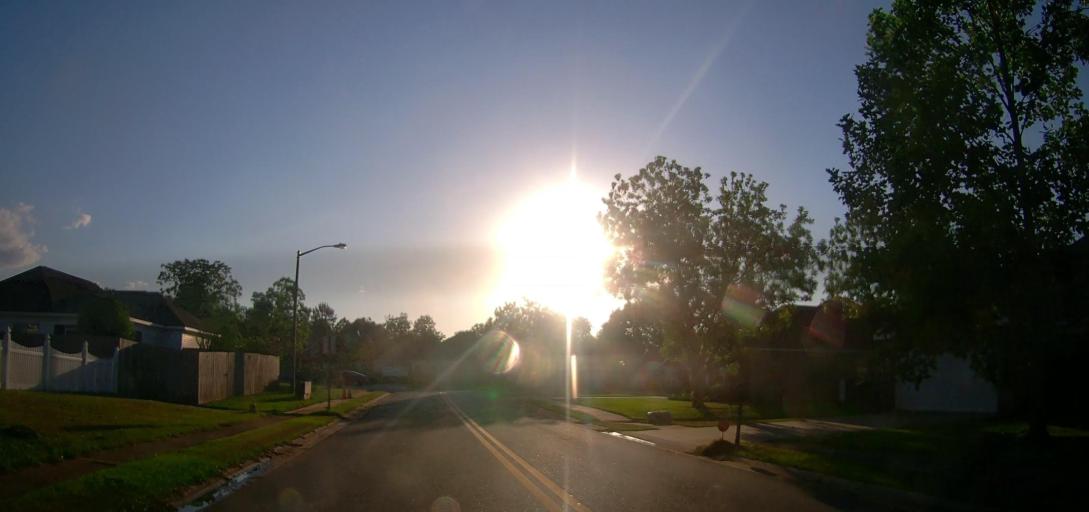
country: US
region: Georgia
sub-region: Houston County
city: Centerville
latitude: 32.6261
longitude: -83.7121
